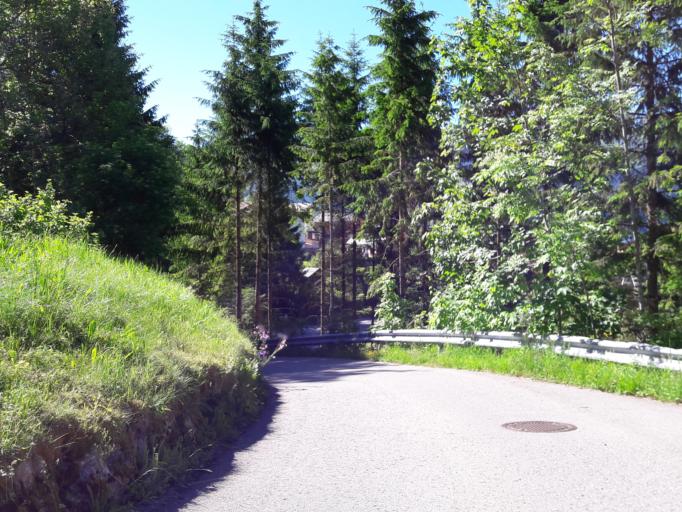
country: AT
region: Vorarlberg
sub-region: Politischer Bezirk Bludenz
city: Raggal
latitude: 47.2093
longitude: 9.8451
